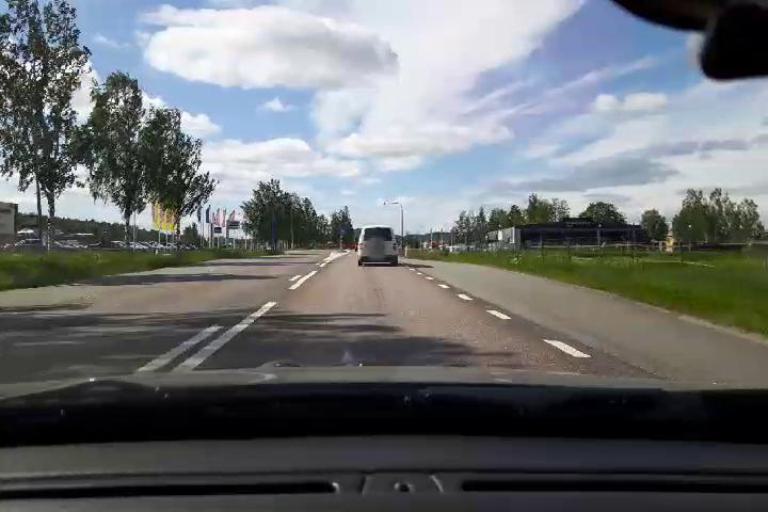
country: SE
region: Gaevleborg
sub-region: Bollnas Kommun
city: Bollnas
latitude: 61.3358
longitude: 16.4005
